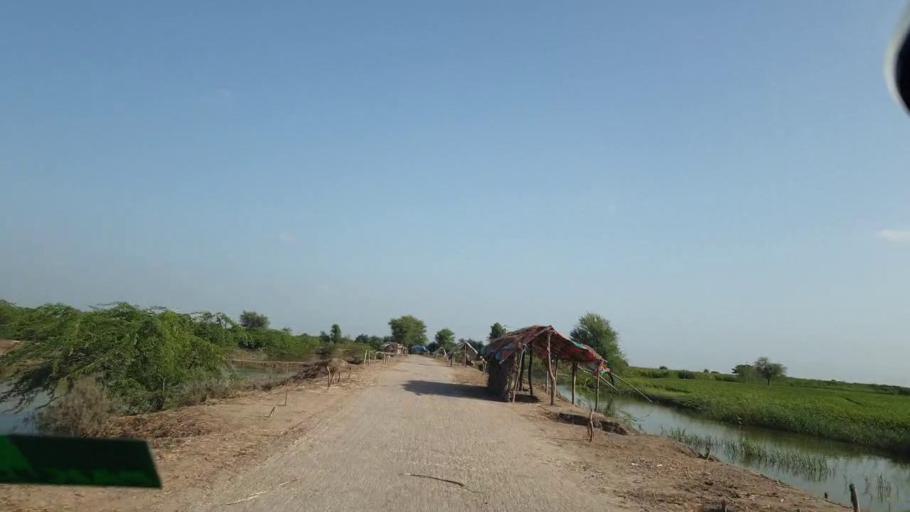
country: PK
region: Sindh
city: Naukot
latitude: 24.7390
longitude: 69.2070
